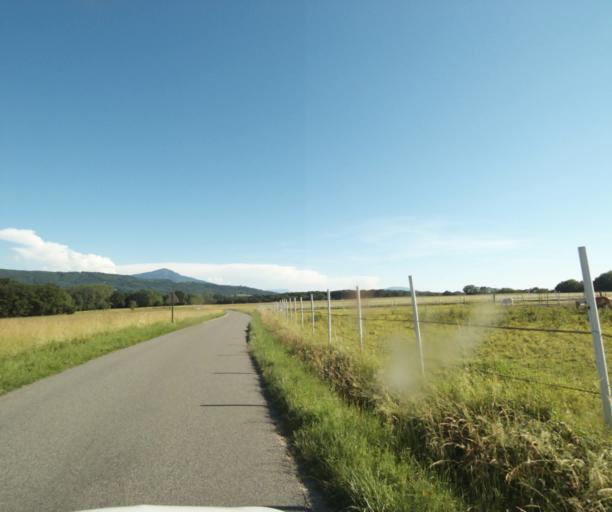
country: FR
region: Rhone-Alpes
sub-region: Departement de la Haute-Savoie
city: Massongy
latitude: 46.3463
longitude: 6.3281
